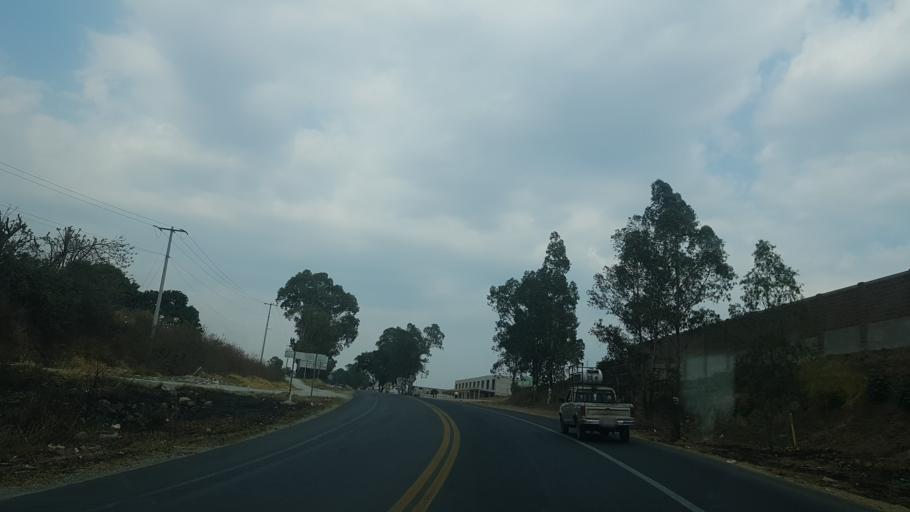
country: MX
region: Puebla
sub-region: Santa Isabel Cholula
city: San Pablo Ahuatempa
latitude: 18.9755
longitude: -98.3739
